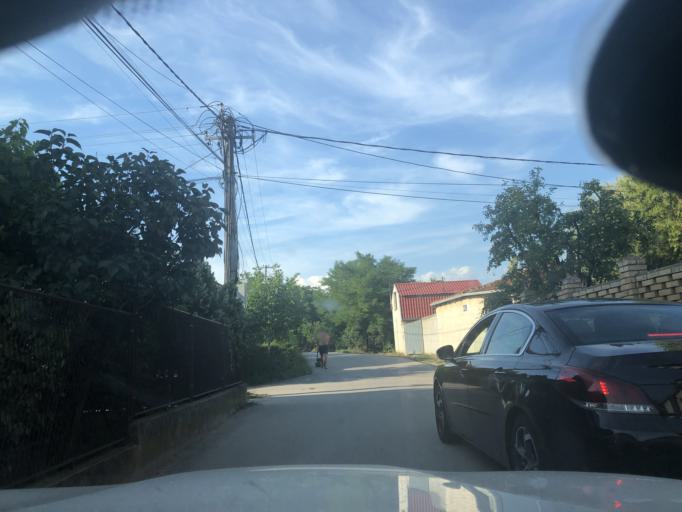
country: RS
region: Central Serbia
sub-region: Nisavski Okrug
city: Nis
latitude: 43.3272
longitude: 21.9556
